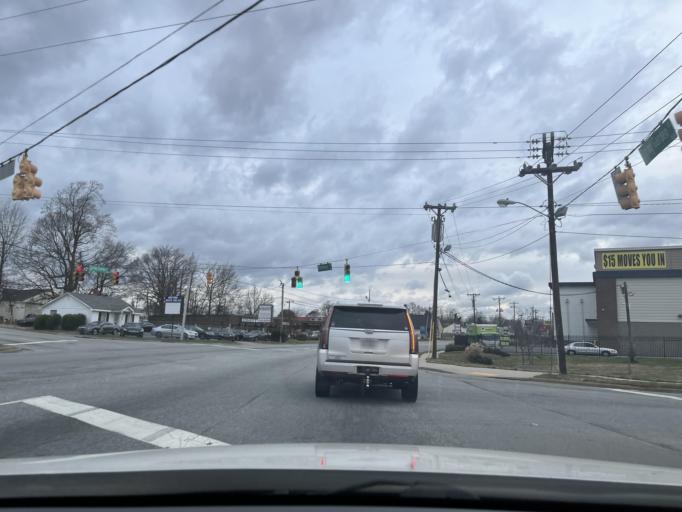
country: US
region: North Carolina
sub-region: Guilford County
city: Greensboro
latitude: 36.0658
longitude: -79.8668
